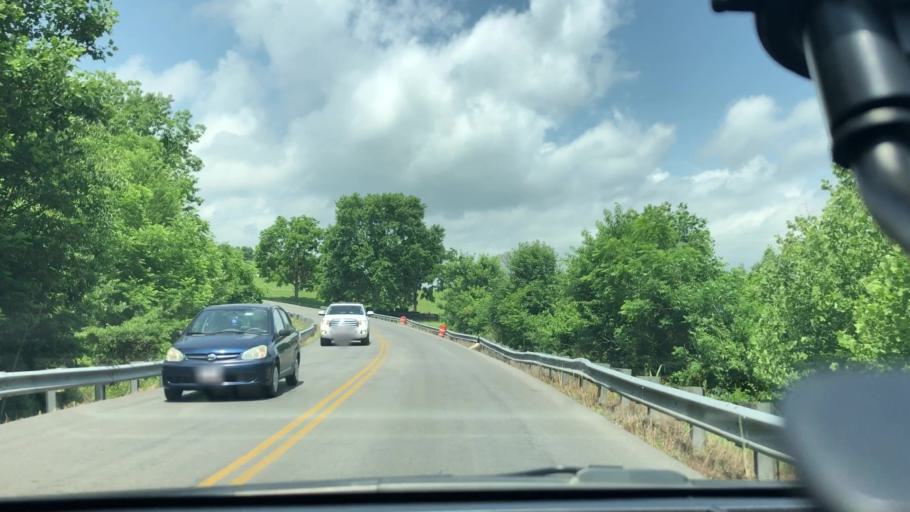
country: US
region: Kentucky
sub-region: Pulaski County
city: Somerset
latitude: 37.0590
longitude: -84.6632
